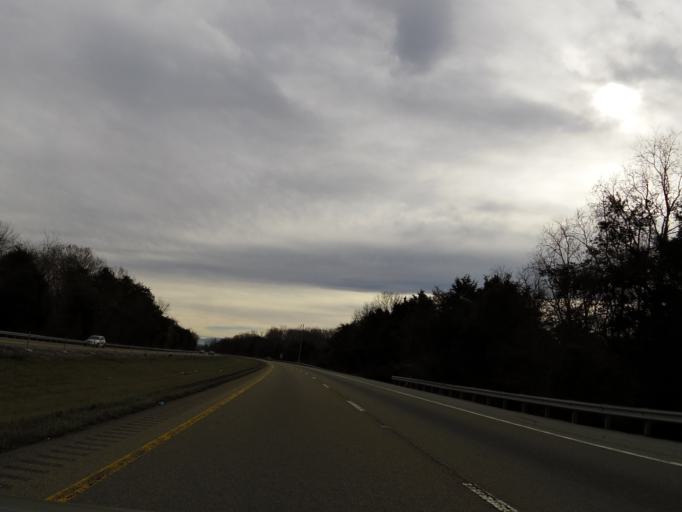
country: US
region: Tennessee
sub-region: Jefferson County
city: Dandridge
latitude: 36.0593
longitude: -83.3749
